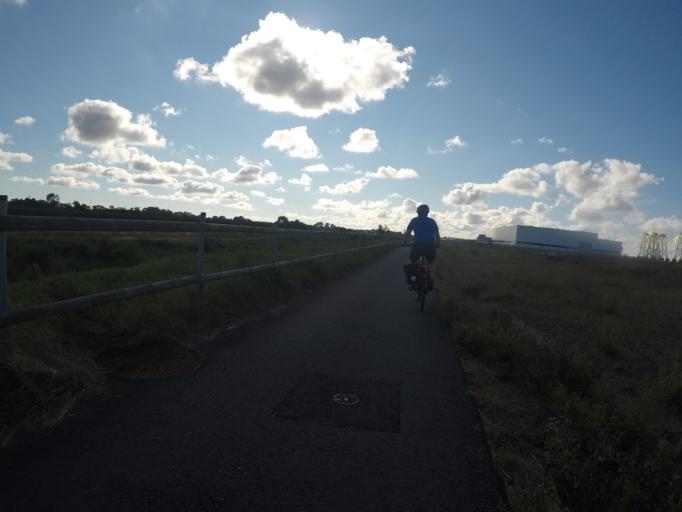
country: DE
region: Lower Saxony
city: Cuxhaven
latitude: 53.8370
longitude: 8.7623
